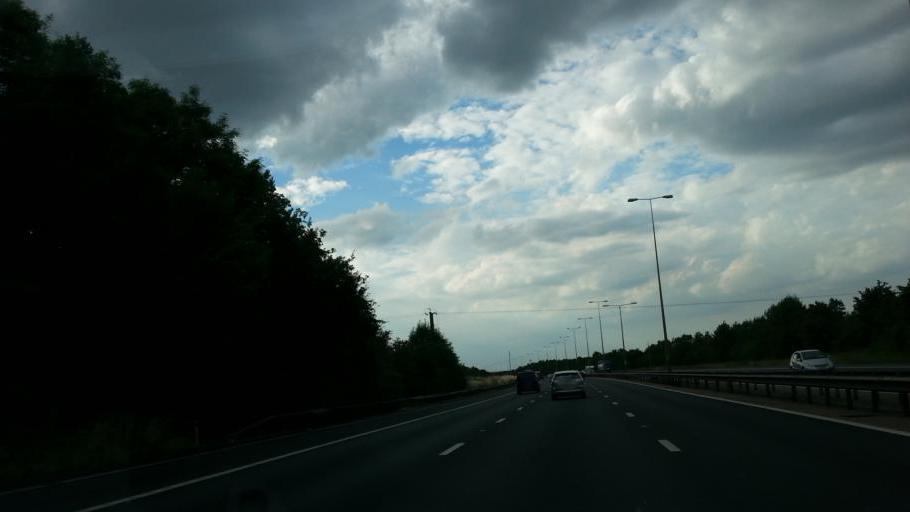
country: GB
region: England
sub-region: Worcestershire
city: Upton upon Severn
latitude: 52.0976
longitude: -2.1861
